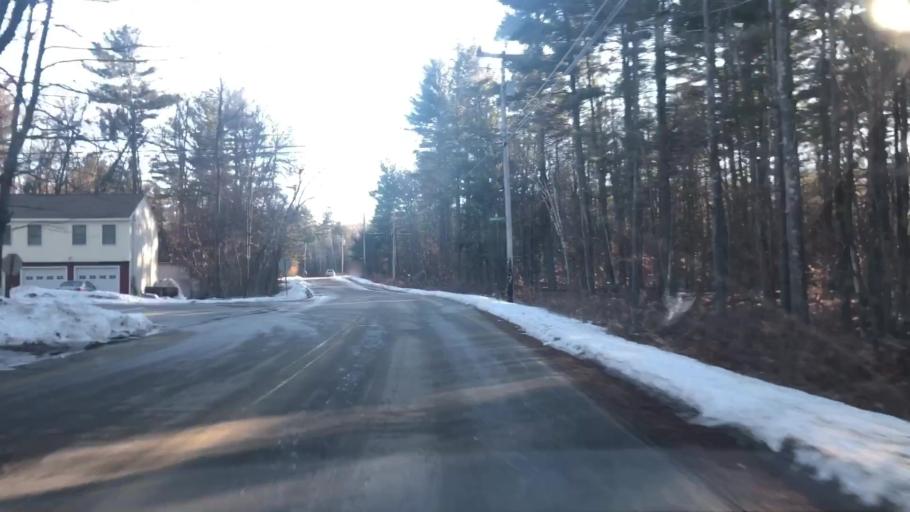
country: US
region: New Hampshire
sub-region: Hillsborough County
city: Milford
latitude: 42.8385
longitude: -71.6811
